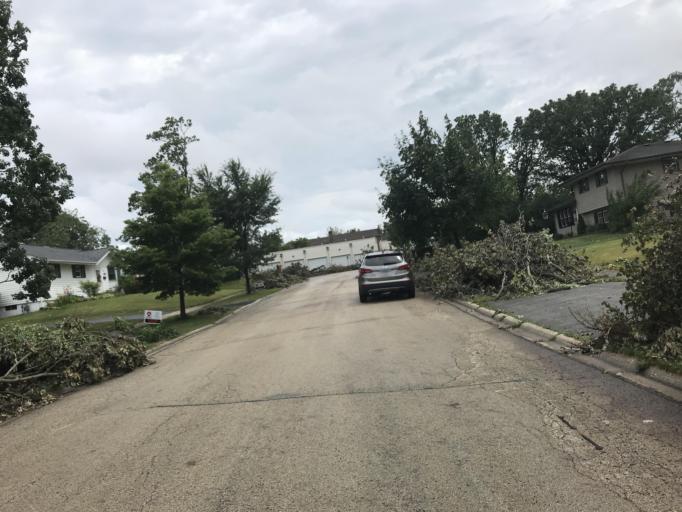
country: US
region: Illinois
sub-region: DuPage County
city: Woodridge
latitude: 41.7436
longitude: -88.0452
